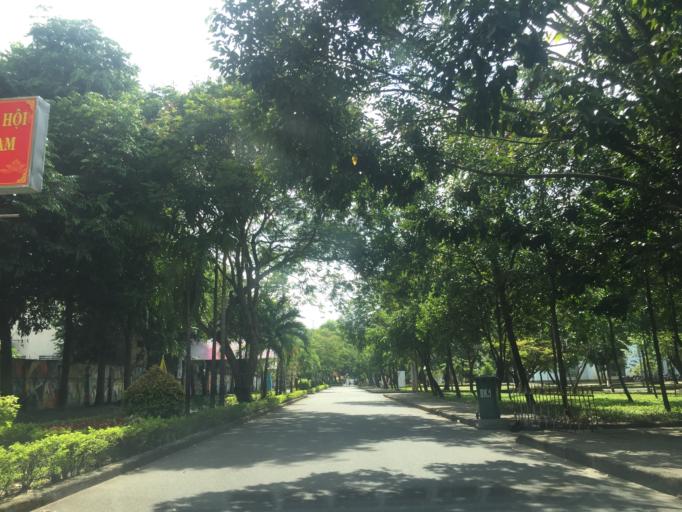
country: VN
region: Da Nang
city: Lien Chieu
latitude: 16.0745
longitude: 108.1521
